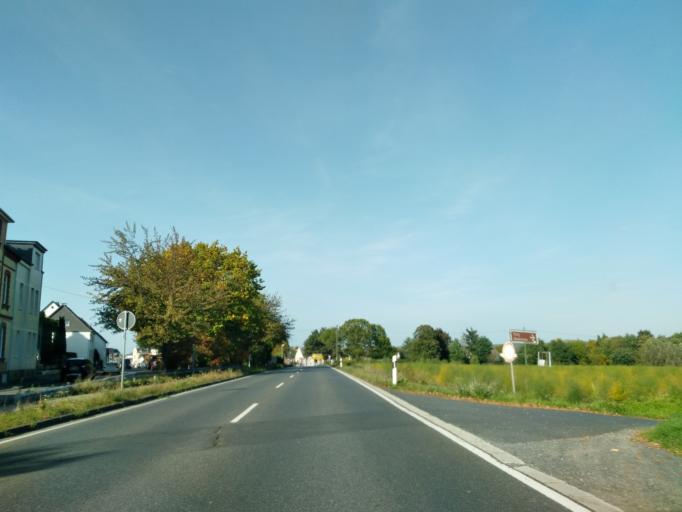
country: DE
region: North Rhine-Westphalia
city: Sankt Augustin
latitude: 50.7692
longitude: 7.2145
